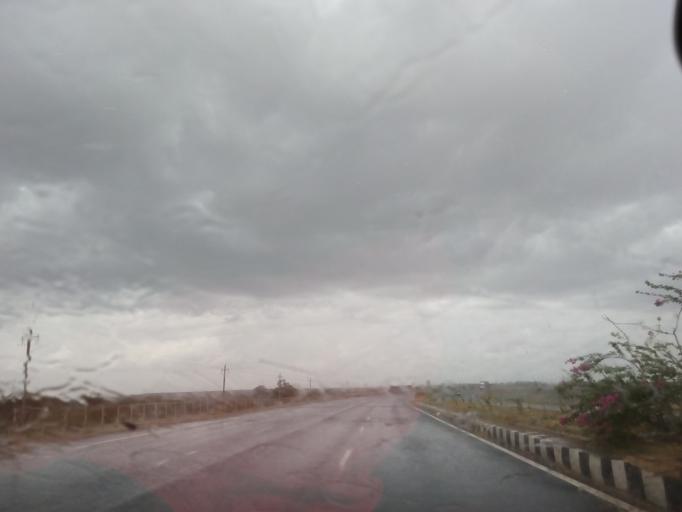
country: IN
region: Karnataka
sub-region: Chitradurga
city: Chitradurga
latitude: 14.1178
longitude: 76.5191
